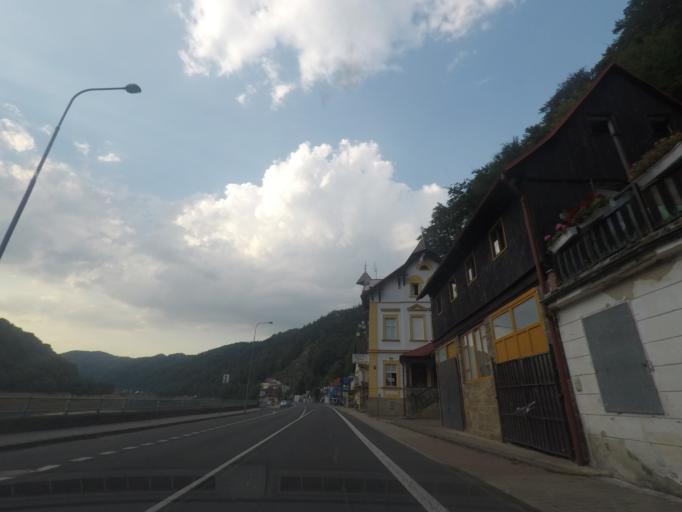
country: DE
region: Saxony
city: Bad Schandau
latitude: 50.8778
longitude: 14.2376
